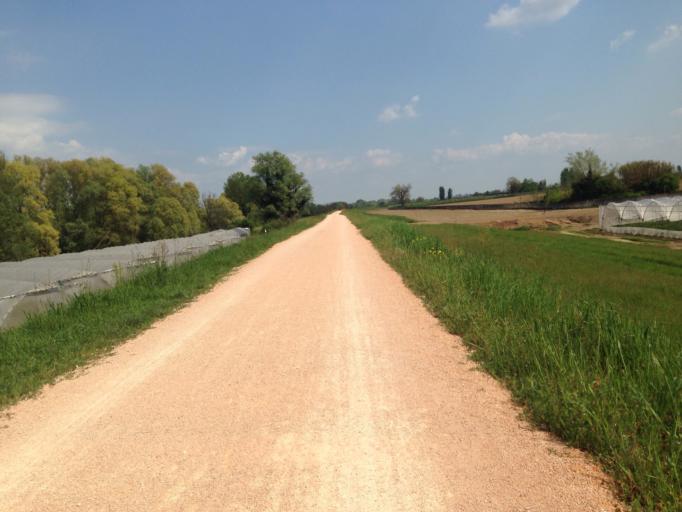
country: IT
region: Veneto
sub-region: Provincia di Verona
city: San Martino Buon Albergo
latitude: 45.3828
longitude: 11.0861
